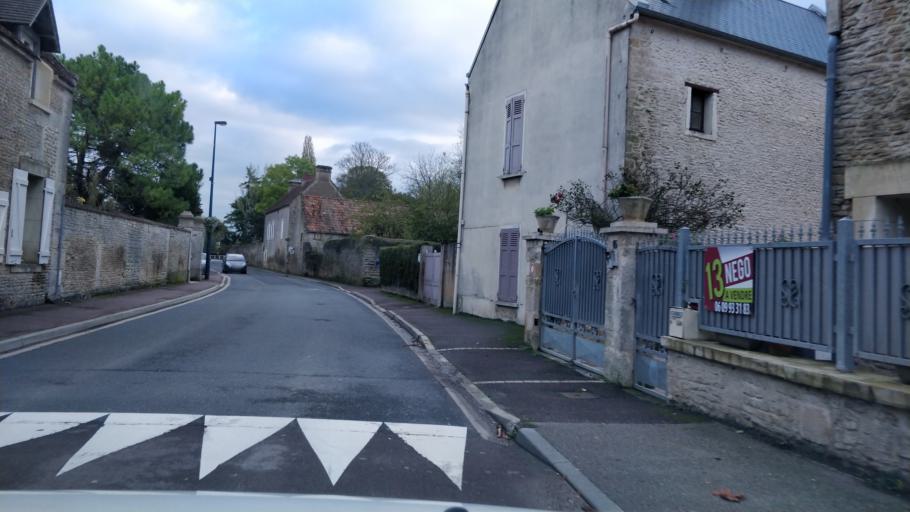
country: FR
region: Lower Normandy
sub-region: Departement du Calvados
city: Benouville
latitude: 49.2603
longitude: -0.2864
